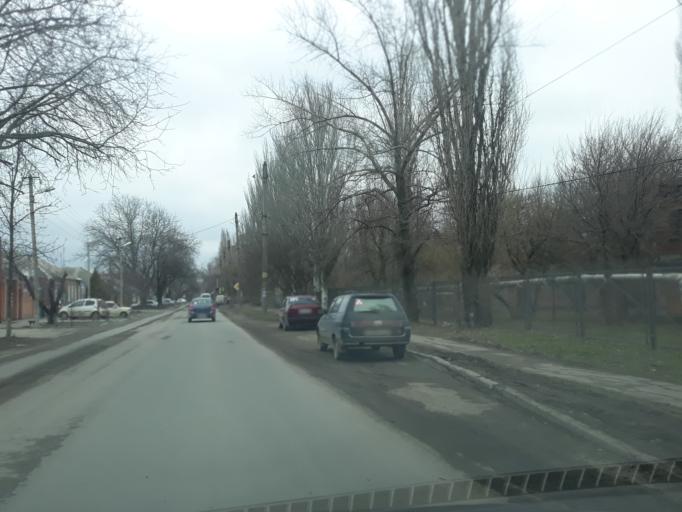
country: RU
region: Rostov
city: Taganrog
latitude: 47.2634
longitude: 38.9131
